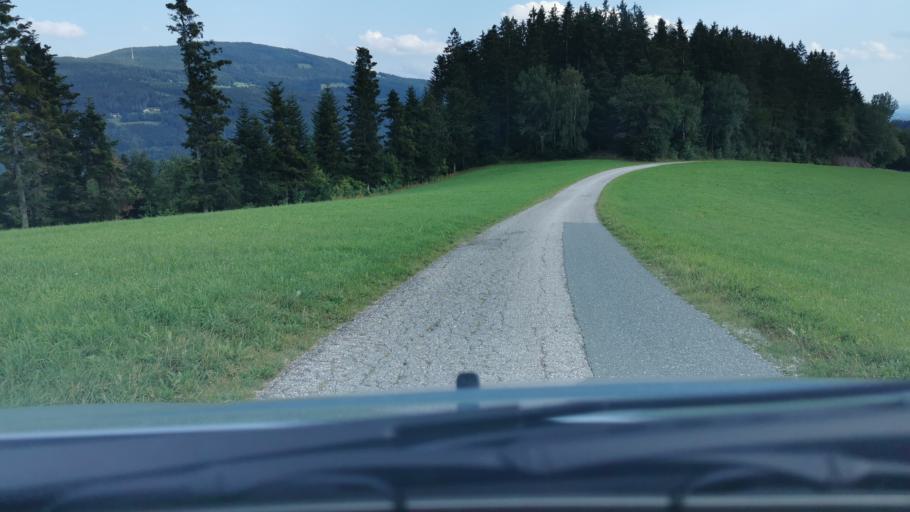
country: AT
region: Styria
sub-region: Politischer Bezirk Weiz
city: Koglhof
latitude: 47.3202
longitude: 15.6700
